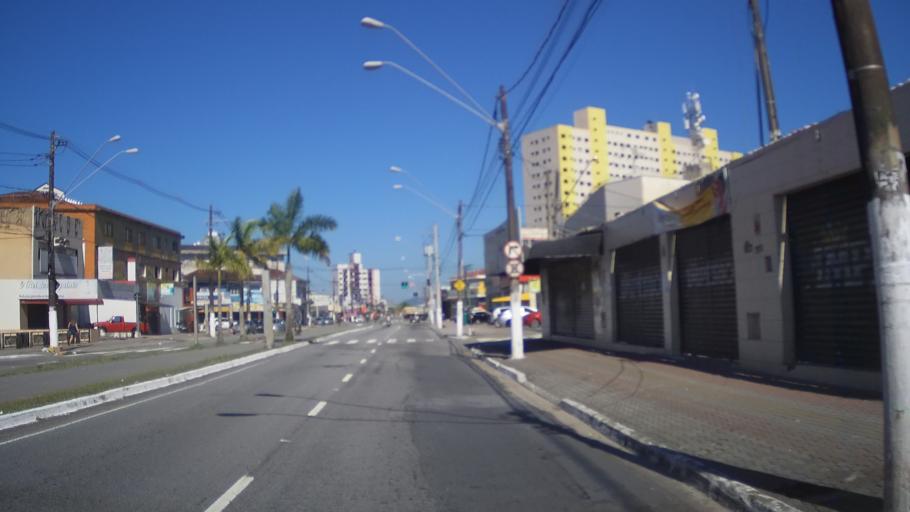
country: BR
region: Sao Paulo
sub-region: Praia Grande
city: Praia Grande
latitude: -24.0250
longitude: -46.4771
